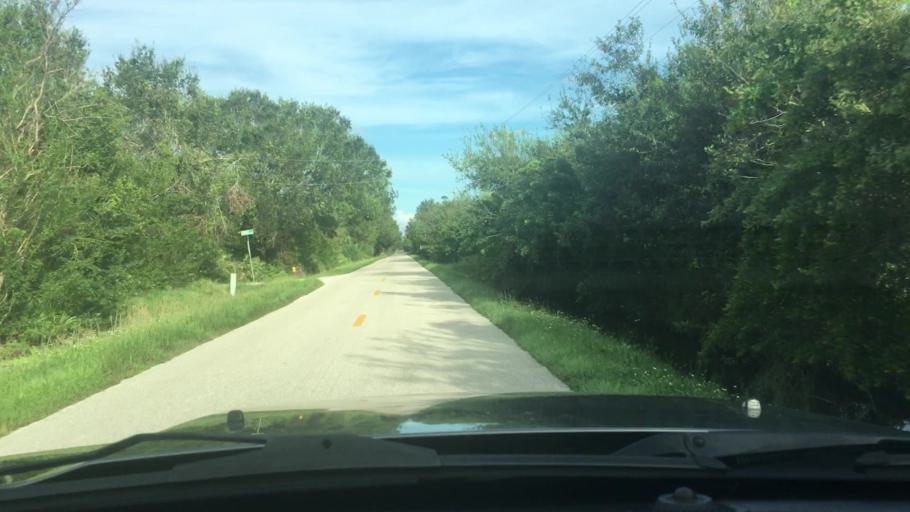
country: US
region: Florida
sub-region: Highlands County
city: Sebring
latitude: 27.4628
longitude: -81.2362
